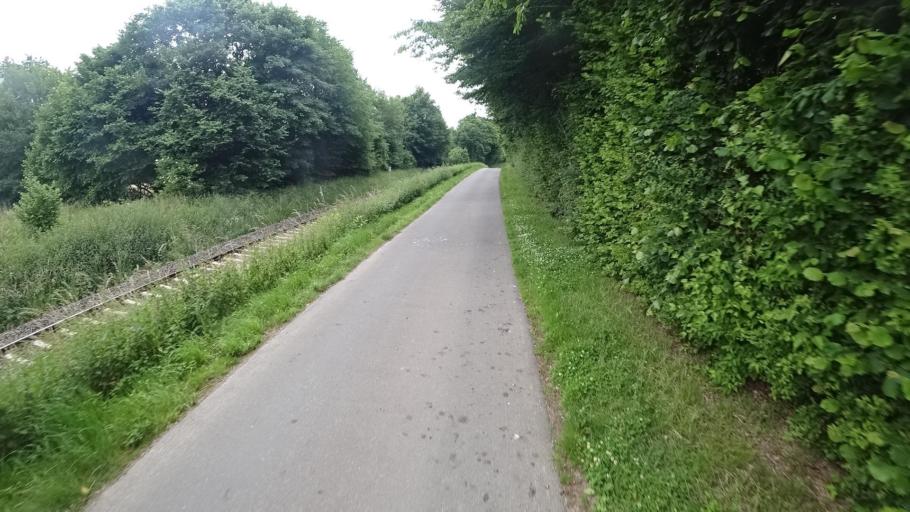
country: DE
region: Rheinland-Pfalz
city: Bachenberg
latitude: 50.7130
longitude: 7.6602
